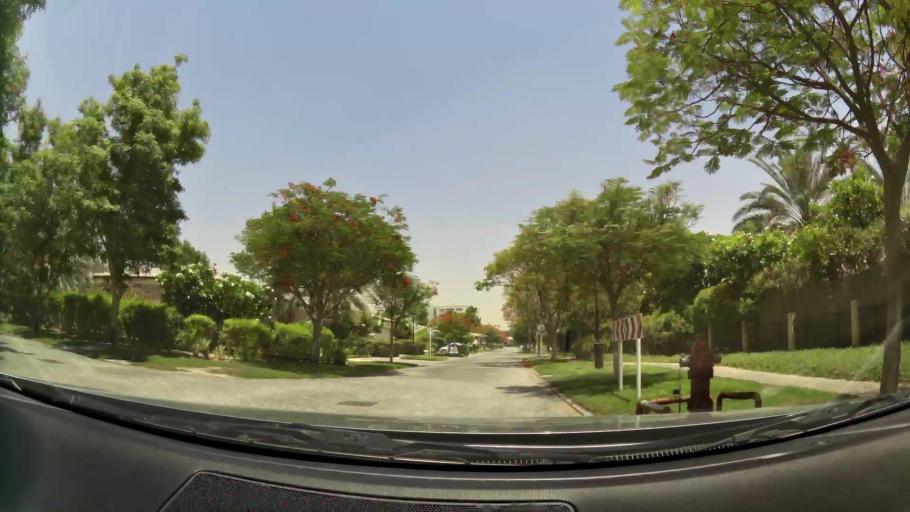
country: AE
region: Dubai
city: Dubai
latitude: 25.0004
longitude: 55.1637
